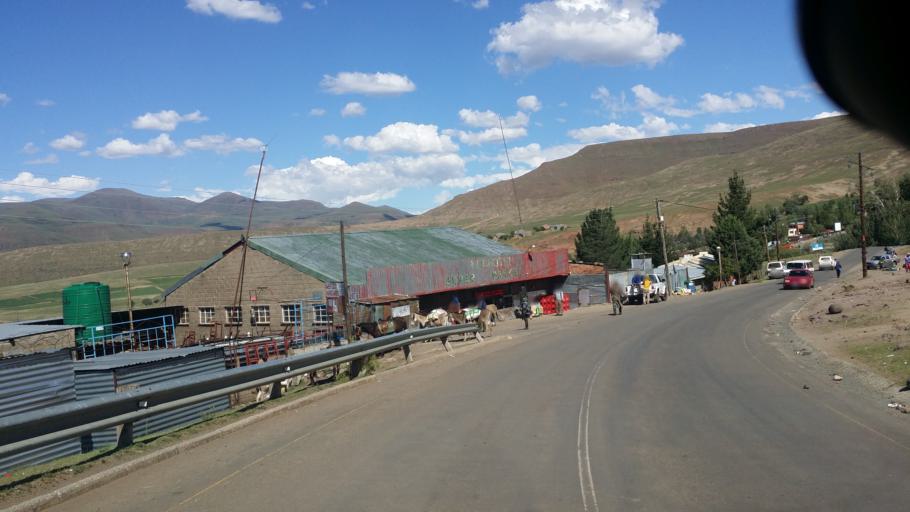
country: LS
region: Mokhotlong
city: Mokhotlong
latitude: -29.2883
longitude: 29.0705
